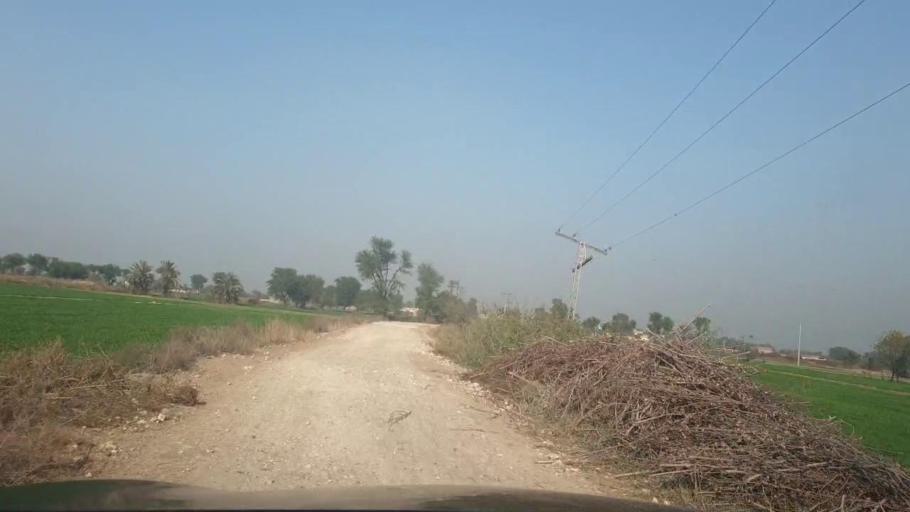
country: PK
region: Sindh
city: Ubauro
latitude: 28.0995
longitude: 69.8423
